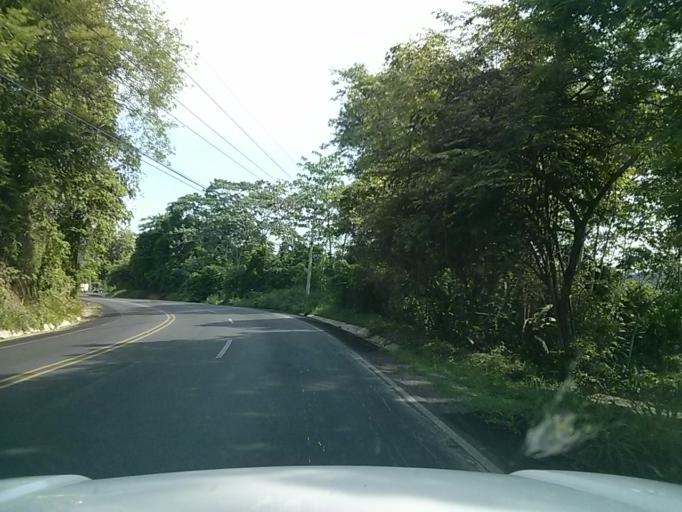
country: CR
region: Puntarenas
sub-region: Canton de Garabito
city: Jaco
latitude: 9.6741
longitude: -84.6417
